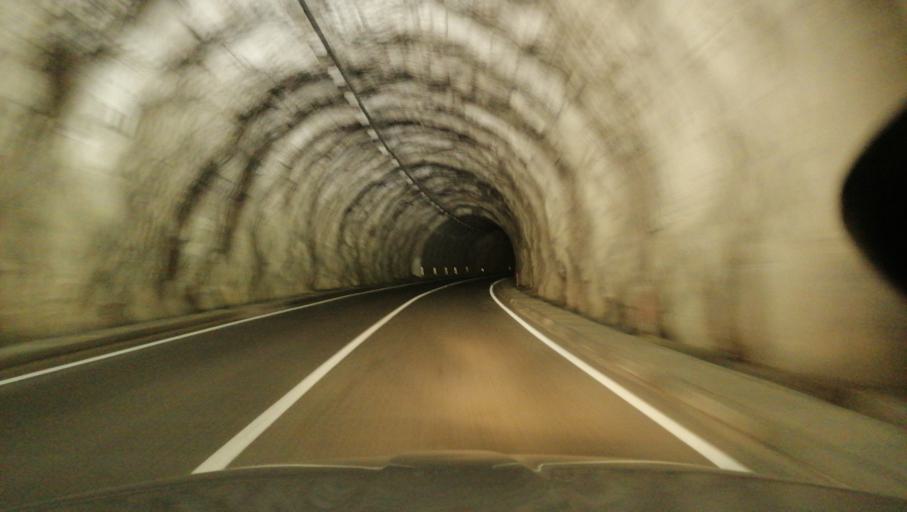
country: BA
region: Republika Srpska
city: Visegrad
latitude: 43.7540
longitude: 19.2431
